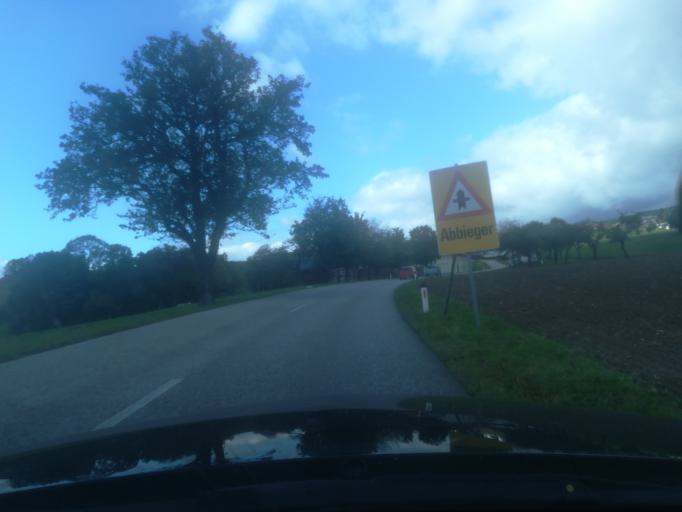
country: AT
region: Upper Austria
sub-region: Linz Stadt
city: Linz
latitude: 48.3495
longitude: 14.2654
